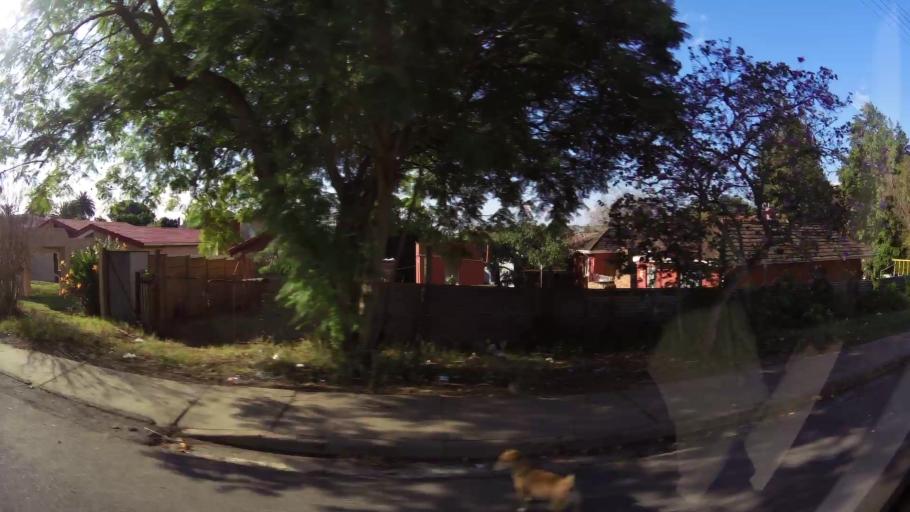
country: ZA
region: Eastern Cape
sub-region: Nelson Mandela Bay Metropolitan Municipality
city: Uitenhage
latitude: -33.7626
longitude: 25.4053
